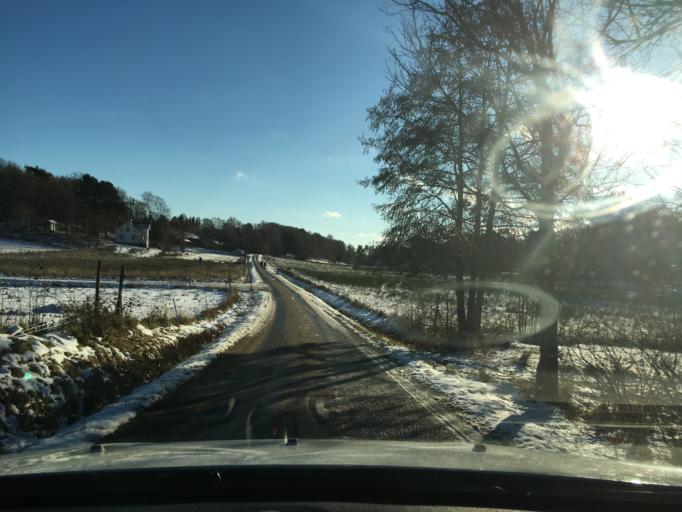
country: SE
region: Vaestra Goetaland
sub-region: Tjorns Kommun
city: Myggenas
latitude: 58.0910
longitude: 11.7720
